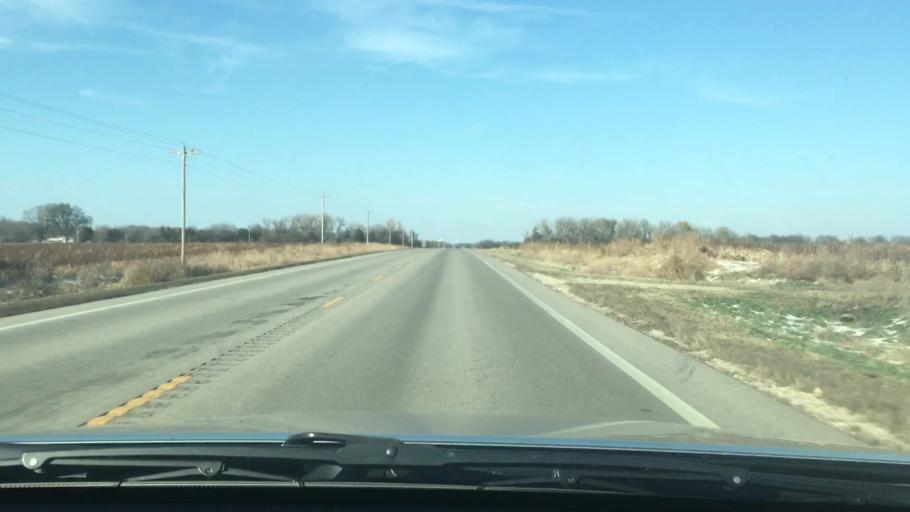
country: US
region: Kansas
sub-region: Rice County
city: Lyons
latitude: 38.3004
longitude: -98.2019
